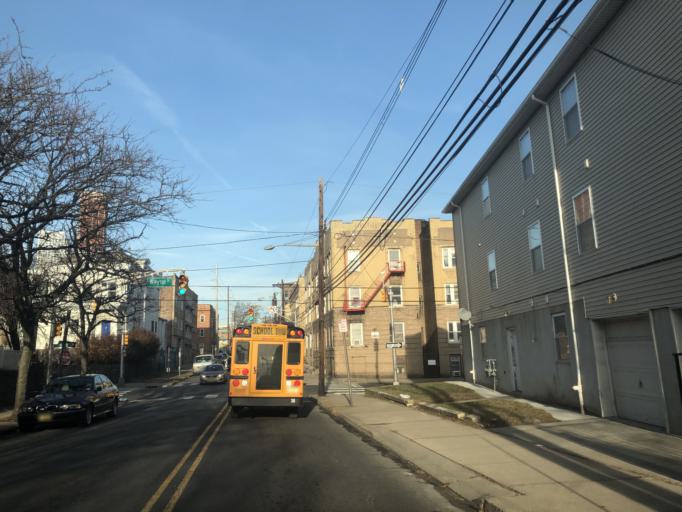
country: US
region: New Jersey
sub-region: Hudson County
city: Jersey City
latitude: 40.7250
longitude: -74.0631
